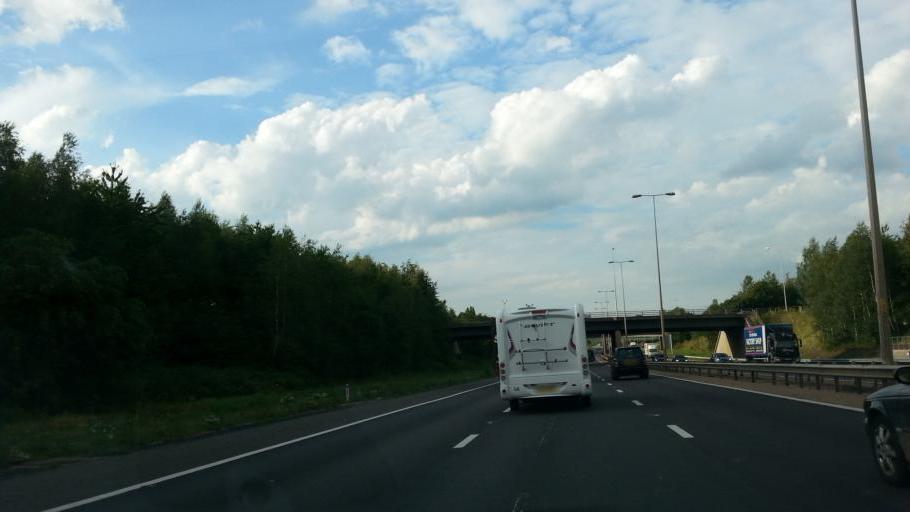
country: GB
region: England
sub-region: Worcestershire
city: Fernhill Heath
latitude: 52.2109
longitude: -2.1589
